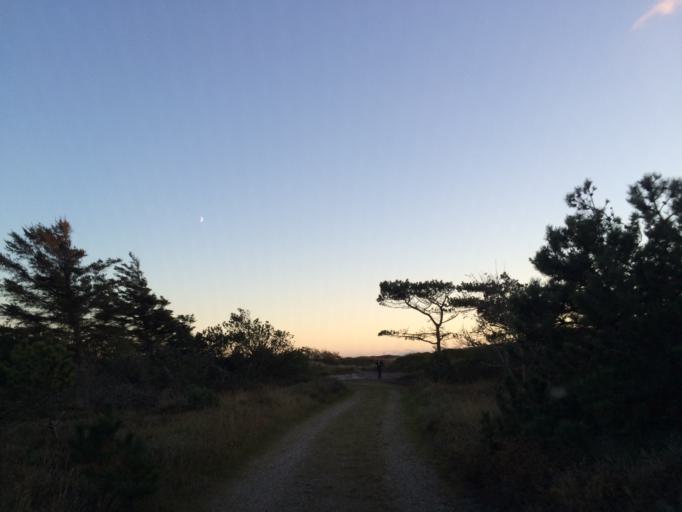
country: DK
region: Central Jutland
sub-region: Holstebro Kommune
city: Ulfborg
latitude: 56.3027
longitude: 8.1335
